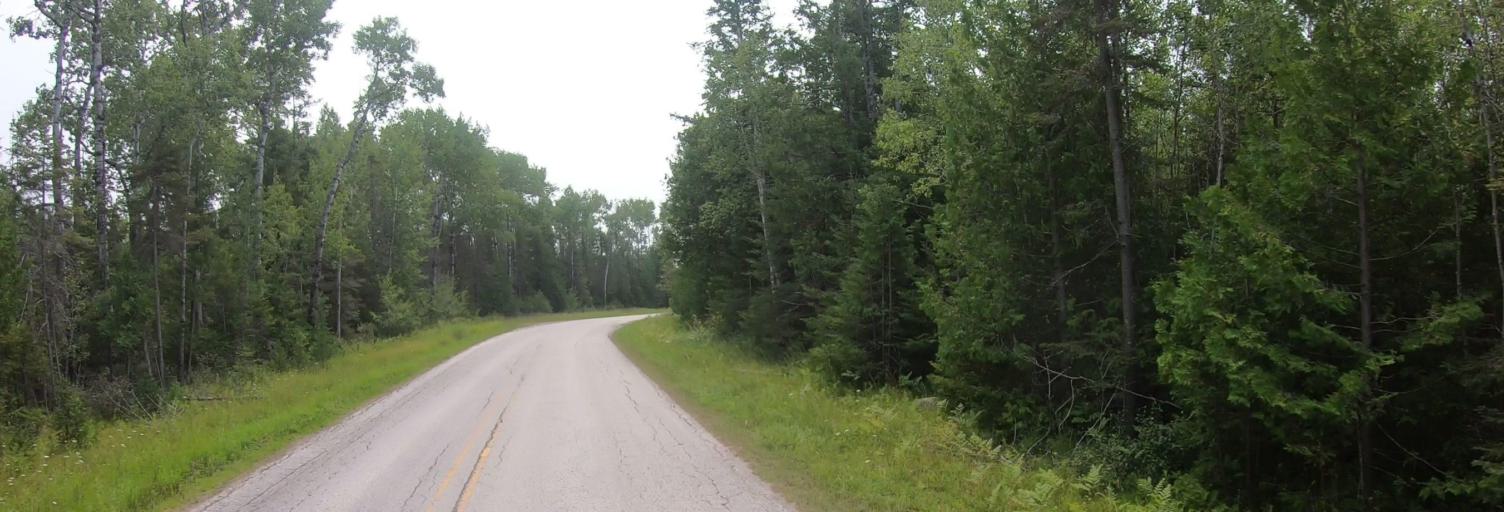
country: CA
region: Ontario
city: Thessalon
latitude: 46.0650
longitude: -83.6648
